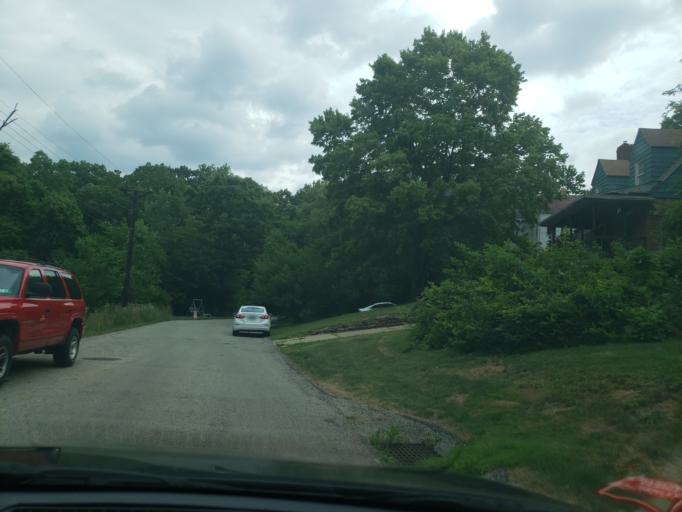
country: US
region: Pennsylvania
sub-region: Allegheny County
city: Ben Avon
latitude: 40.5179
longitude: -80.0869
